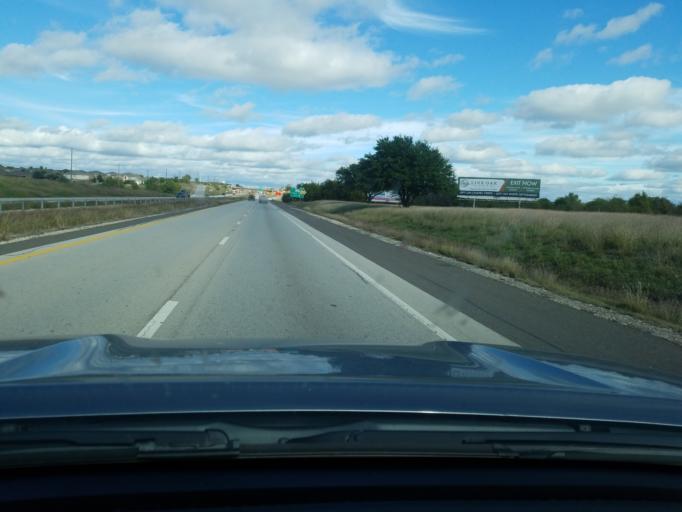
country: US
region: Texas
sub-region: Tarrant County
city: White Settlement
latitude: 32.7259
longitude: -97.5111
